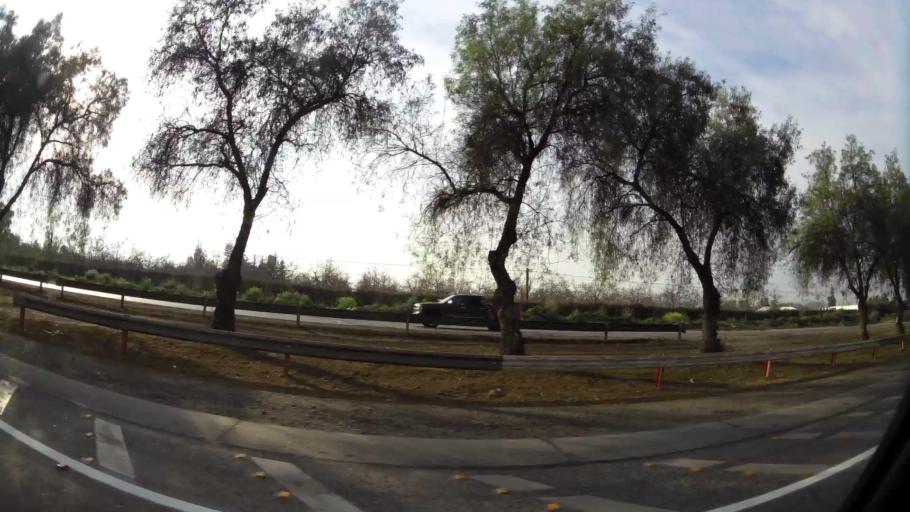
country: CL
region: Santiago Metropolitan
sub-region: Provincia de Talagante
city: Penaflor
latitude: -33.5934
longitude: -70.8426
